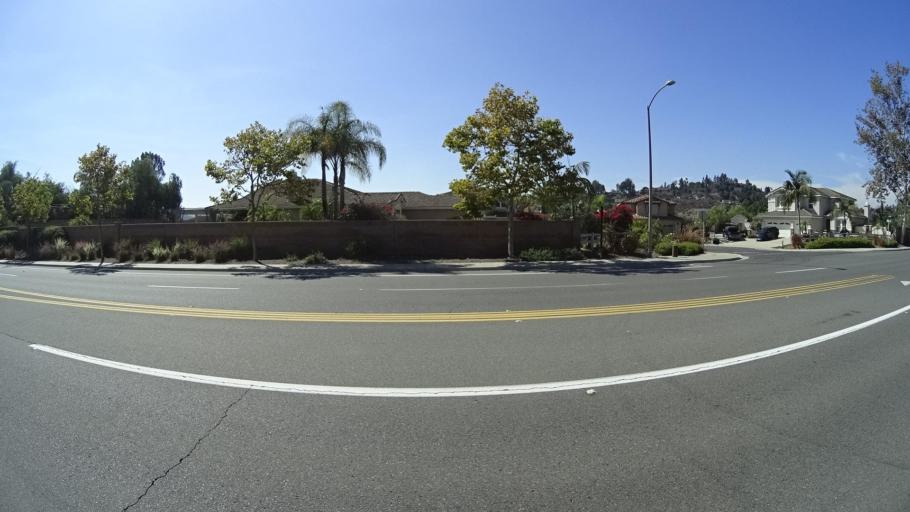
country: US
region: California
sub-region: San Diego County
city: Rancho San Diego
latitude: 32.7664
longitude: -116.9237
